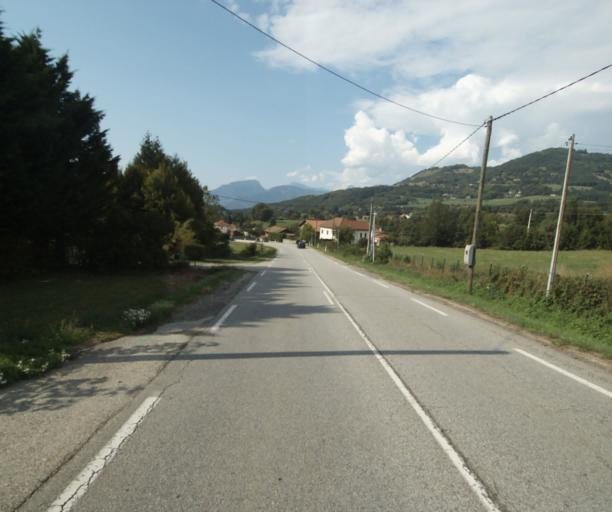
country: FR
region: Rhone-Alpes
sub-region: Departement de l'Isere
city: Brie-et-Angonnes
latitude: 45.1315
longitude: 5.7764
